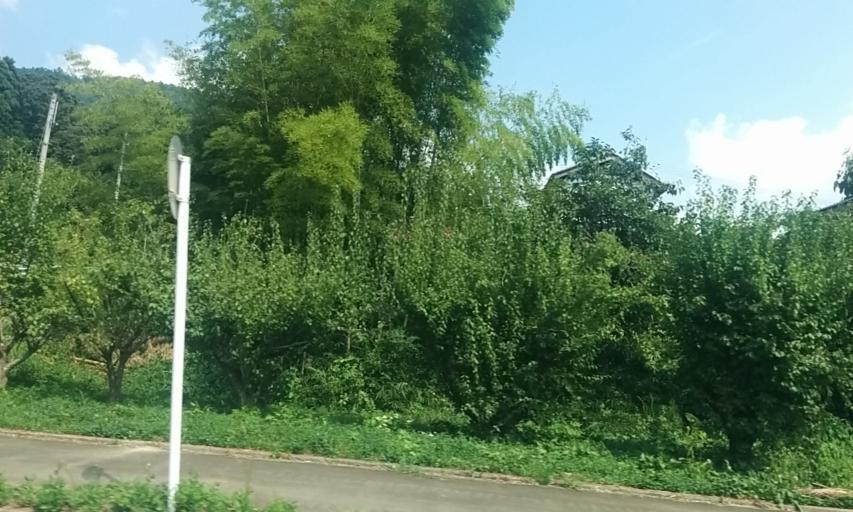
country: JP
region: Kyoto
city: Fukuchiyama
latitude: 35.3489
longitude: 135.1148
